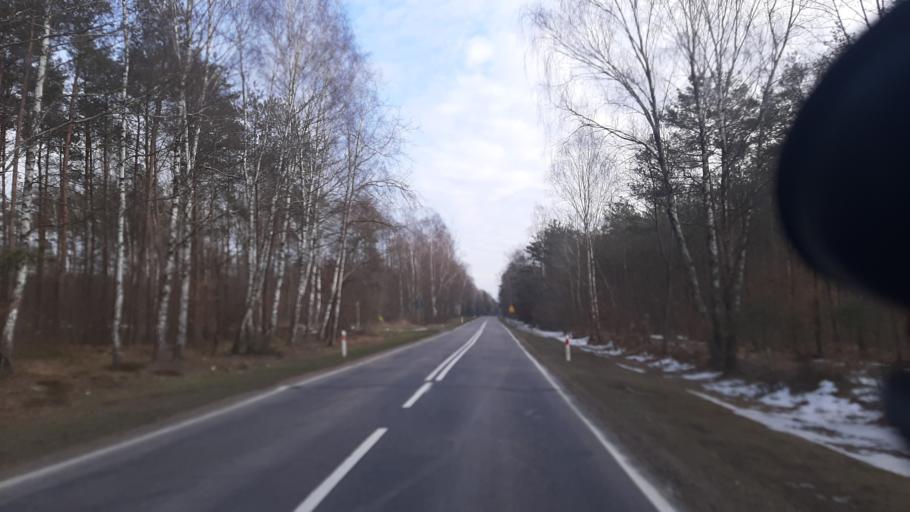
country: PL
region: Lublin Voivodeship
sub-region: Powiat lubartowski
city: Ostrow Lubelski
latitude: 51.4912
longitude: 22.8152
